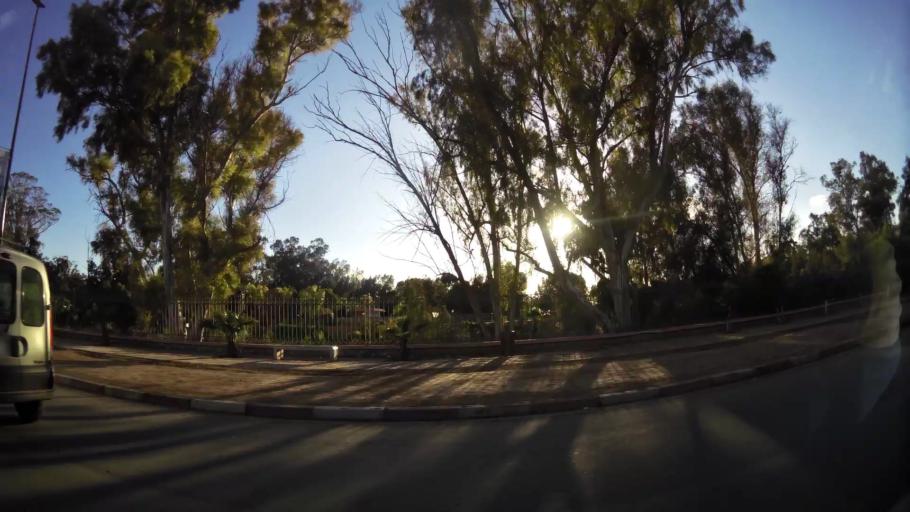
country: MA
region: Marrakech-Tensift-Al Haouz
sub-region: Kelaa-Des-Sraghna
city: Sidi Abdallah
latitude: 32.2316
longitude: -7.9575
